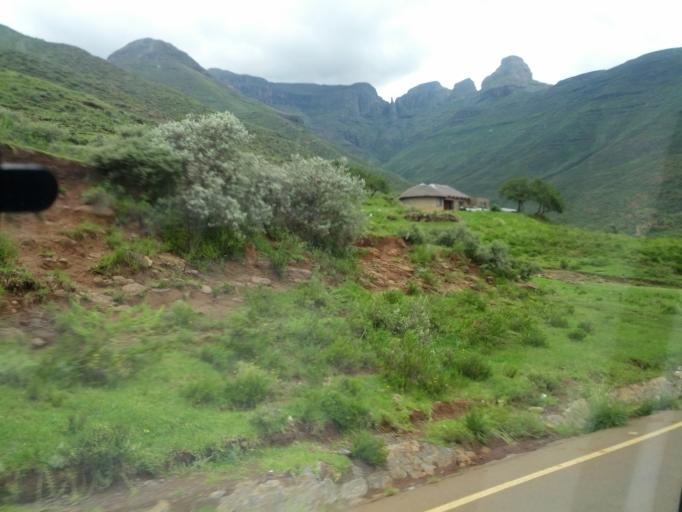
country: LS
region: Butha-Buthe
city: Butha-Buthe
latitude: -29.0452
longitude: 28.3142
